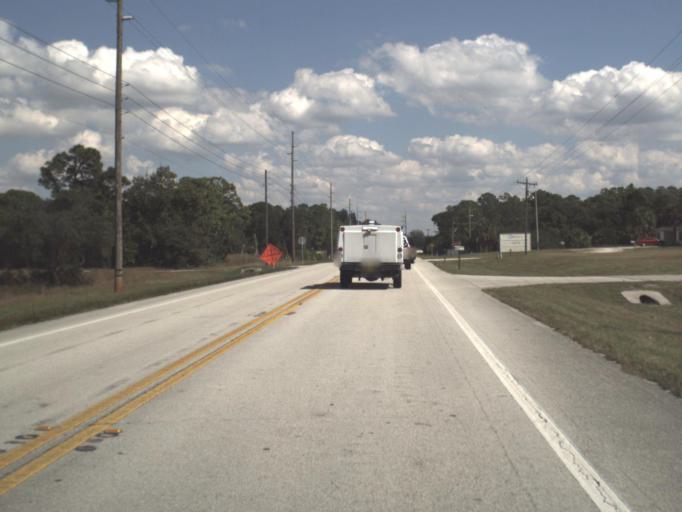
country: US
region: Florida
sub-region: Highlands County
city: Sebring
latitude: 27.4334
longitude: -81.3739
